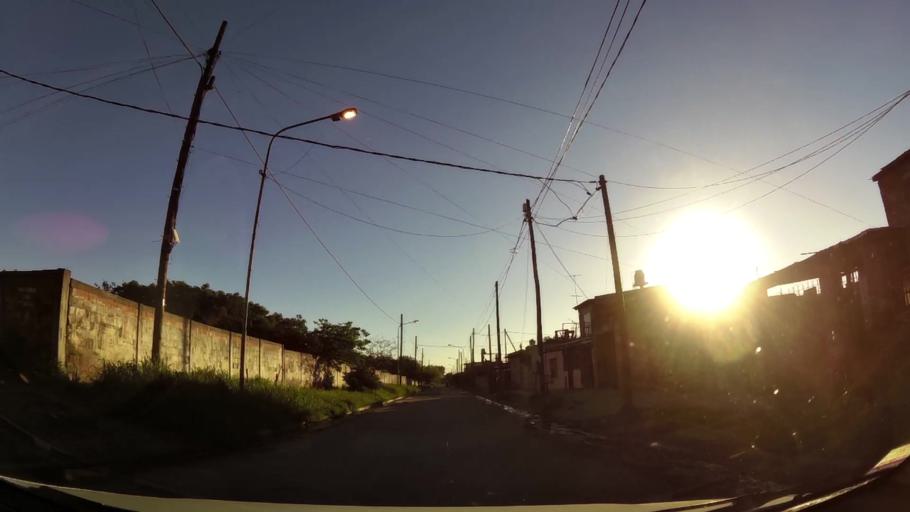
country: AR
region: Buenos Aires
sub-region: Partido de Moron
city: Moron
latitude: -34.7162
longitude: -58.6157
